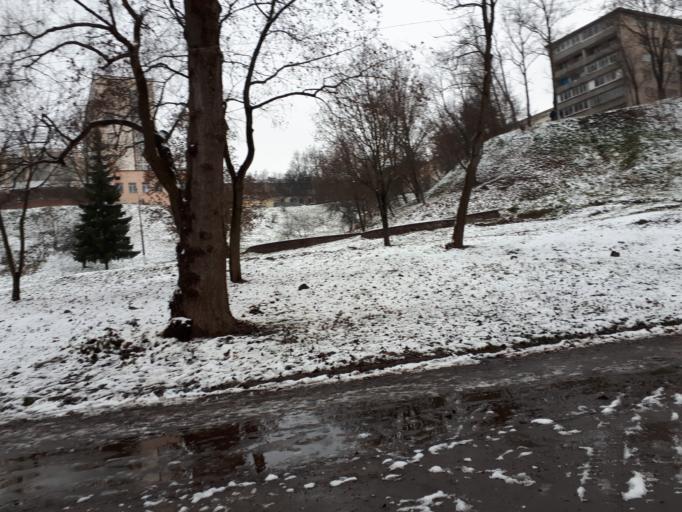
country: BY
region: Vitebsk
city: Vitebsk
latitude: 55.1978
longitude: 30.2105
